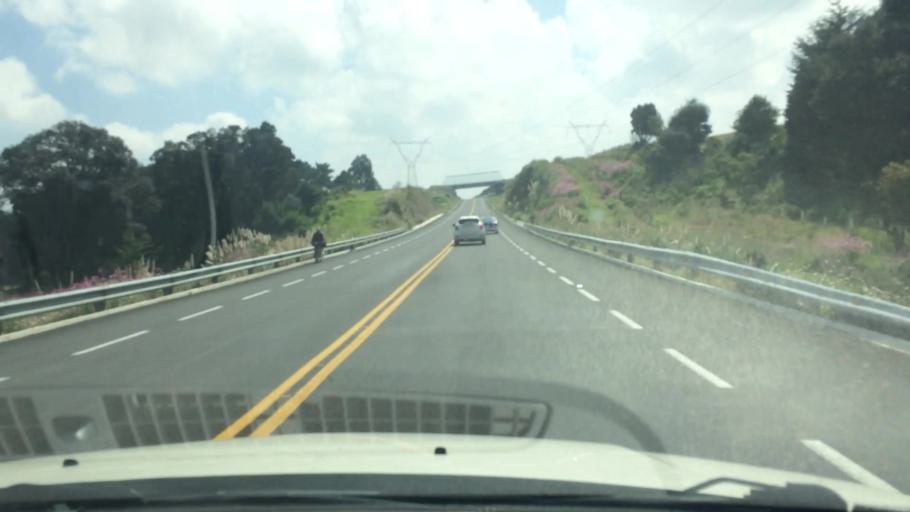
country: MX
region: Mexico
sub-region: Almoloya de Juarez
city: San Pedro de la Hortaliza (Ejido Almoloyan)
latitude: 19.3784
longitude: -99.8523
